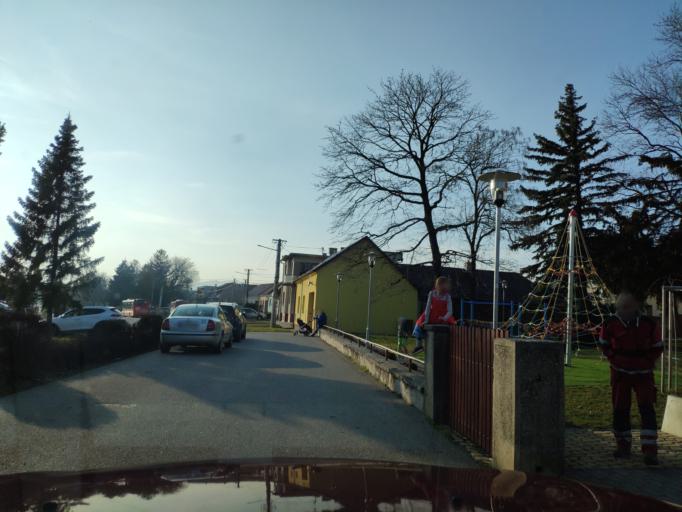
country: SK
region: Bratislavsky
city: Modra
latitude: 48.3346
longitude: 17.3965
